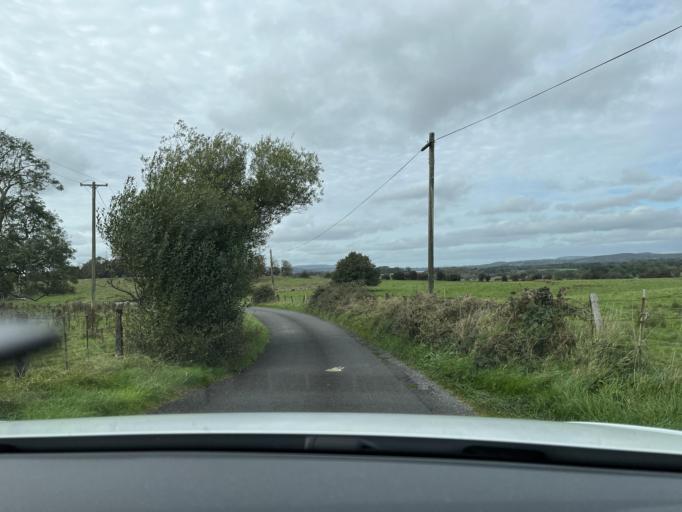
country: IE
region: Connaught
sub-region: Roscommon
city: Boyle
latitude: 53.9724
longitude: -8.2084
